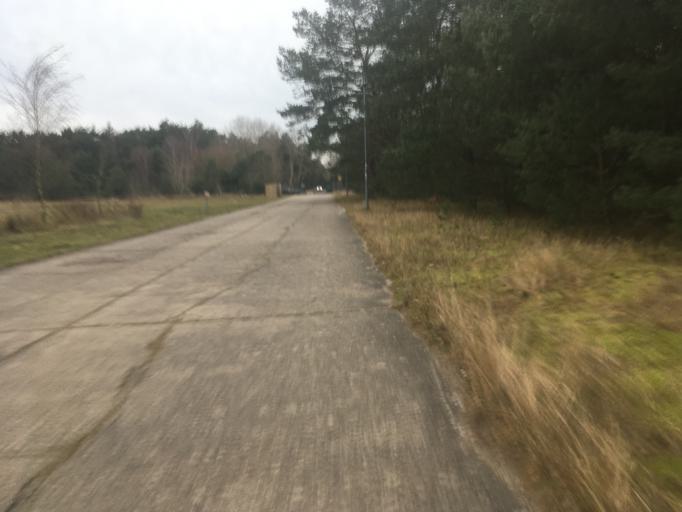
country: DE
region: Mecklenburg-Vorpommern
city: Ostseebad Binz
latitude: 54.4552
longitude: 13.5679
